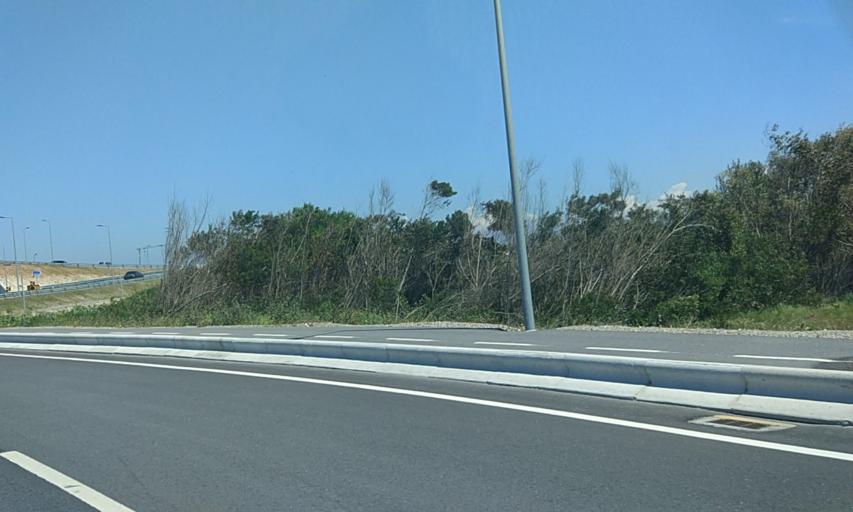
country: PT
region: Aveiro
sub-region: Ilhavo
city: Gafanha da Encarnacao
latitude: 40.6309
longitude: -8.7456
